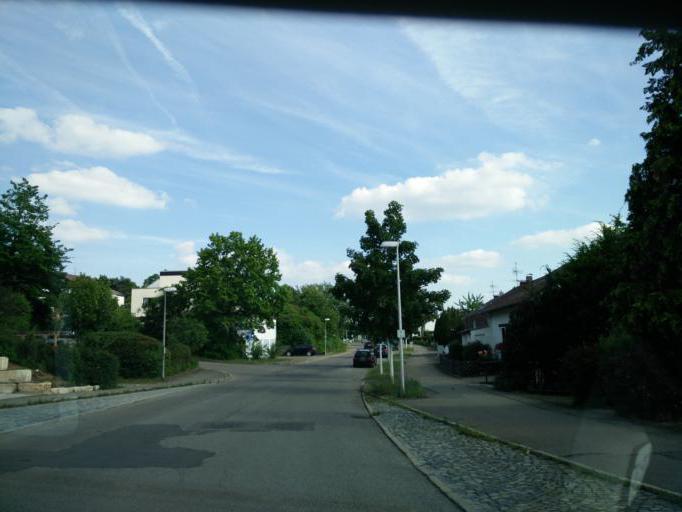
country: DE
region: Baden-Wuerttemberg
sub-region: Tuebingen Region
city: Tuebingen
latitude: 48.5392
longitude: 9.0488
